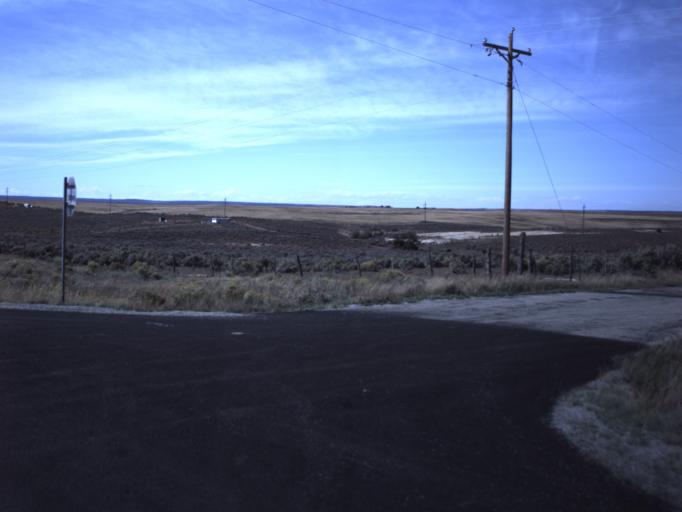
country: US
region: Utah
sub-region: San Juan County
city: Monticello
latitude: 37.8688
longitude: -109.2455
